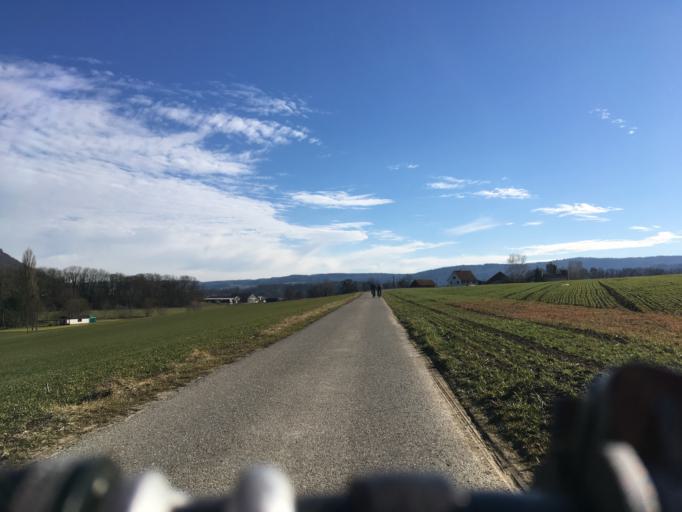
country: CH
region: Schaffhausen
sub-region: Bezirk Stein
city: Ramsen
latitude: 47.6919
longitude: 8.8124
